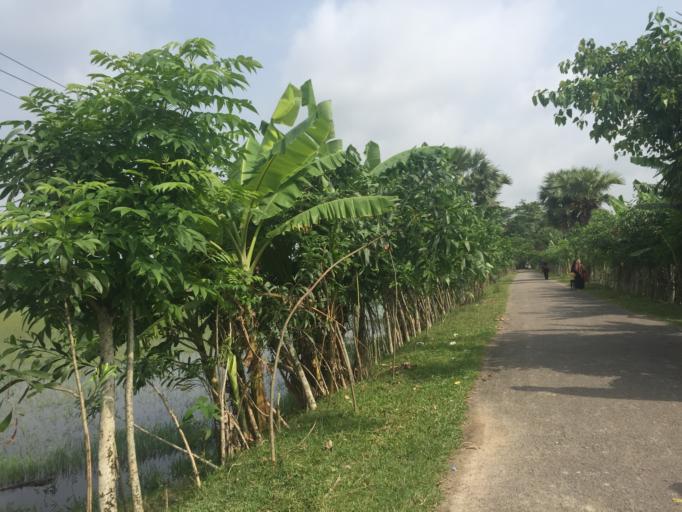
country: BD
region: Barisal
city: Mathba
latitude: 22.2625
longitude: 89.9099
